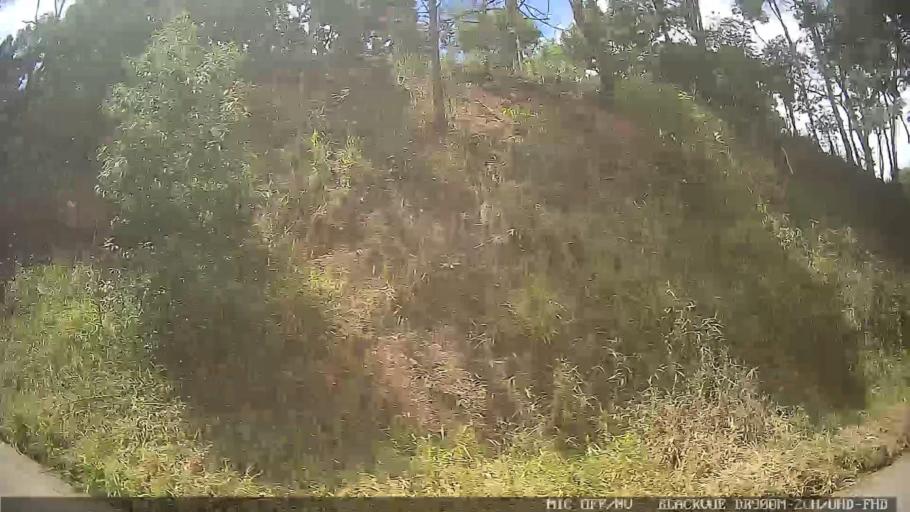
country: BR
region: Sao Paulo
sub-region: Braganca Paulista
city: Braganca Paulista
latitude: -22.8020
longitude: -46.4879
